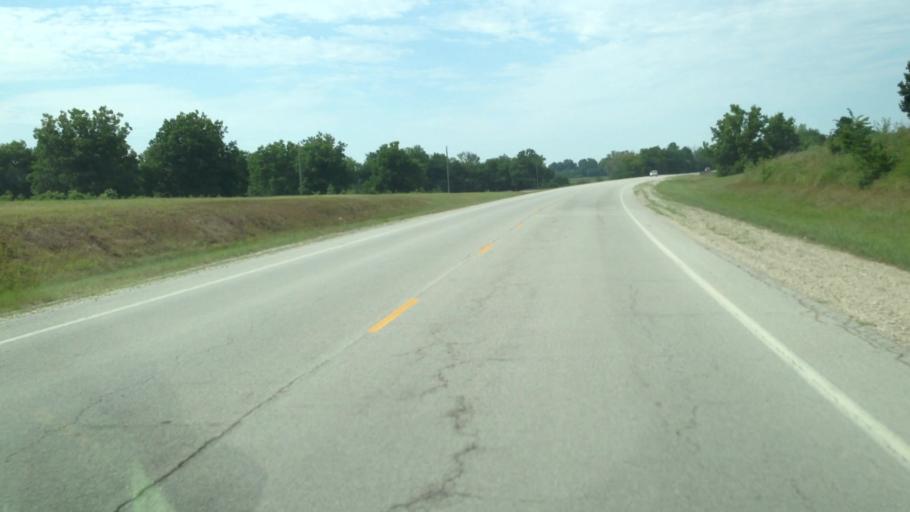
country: US
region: Kansas
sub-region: Labette County
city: Chetopa
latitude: 37.0536
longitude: -95.1021
